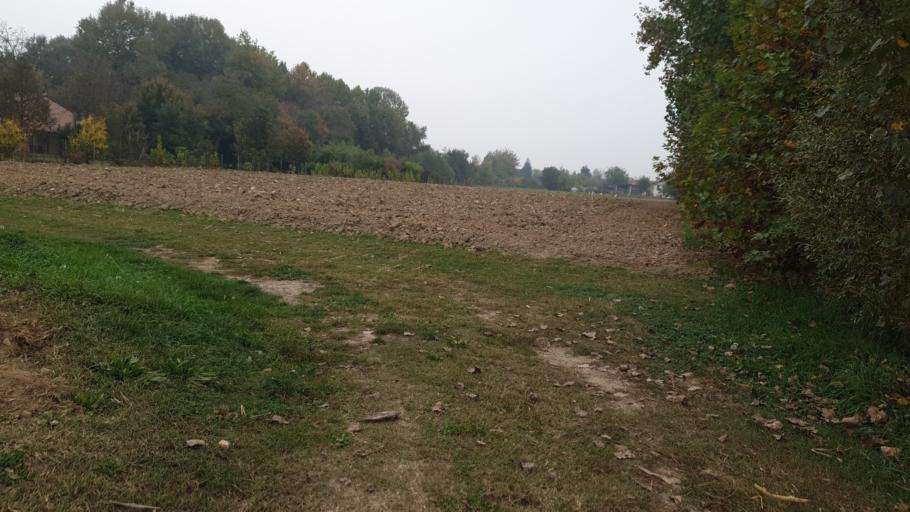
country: IT
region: Veneto
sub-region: Provincia di Padova
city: Bertipaglia
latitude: 45.3195
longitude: 11.8959
